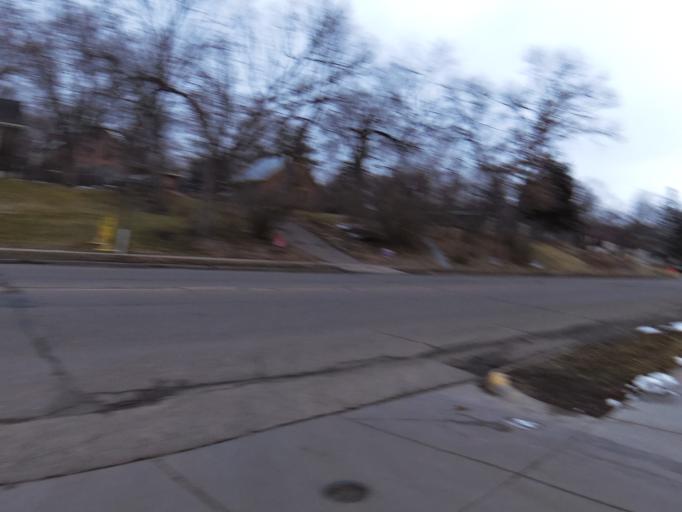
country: US
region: Wisconsin
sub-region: Saint Croix County
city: Hudson
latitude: 44.9811
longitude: -92.7573
